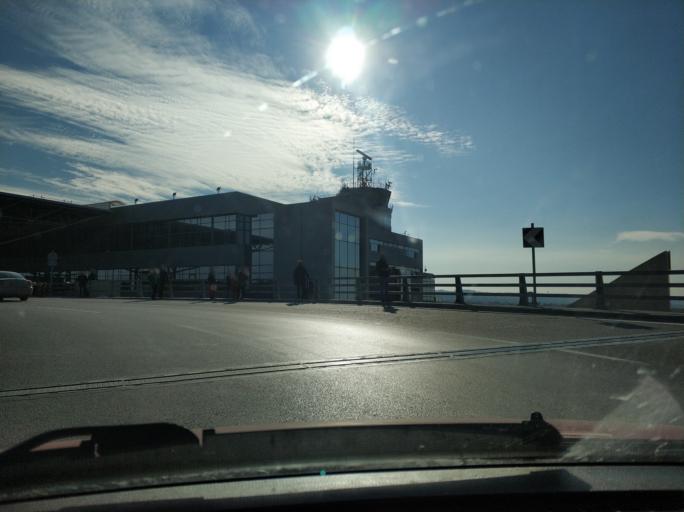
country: GR
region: Central Macedonia
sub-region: Nomos Thessalonikis
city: Neo Rysi
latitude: 40.5252
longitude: 22.9757
